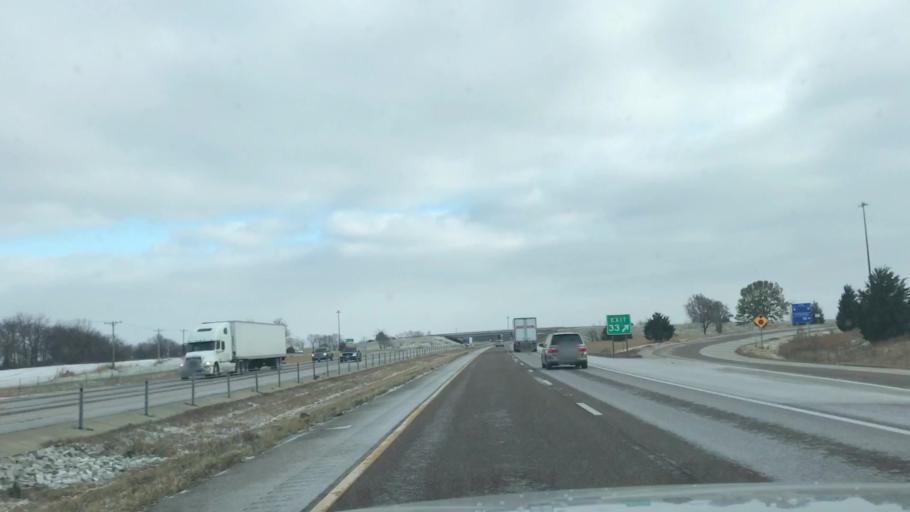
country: US
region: Illinois
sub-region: Madison County
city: Worden
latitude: 38.9288
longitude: -89.8043
